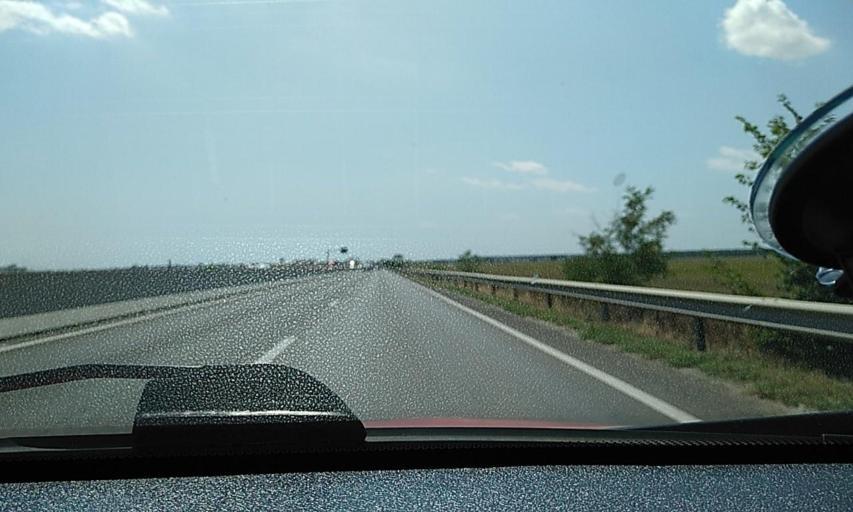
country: RO
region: Prahova
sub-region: Comuna Targsoru Vechi
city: Strejnicu
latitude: 44.9542
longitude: 25.9578
